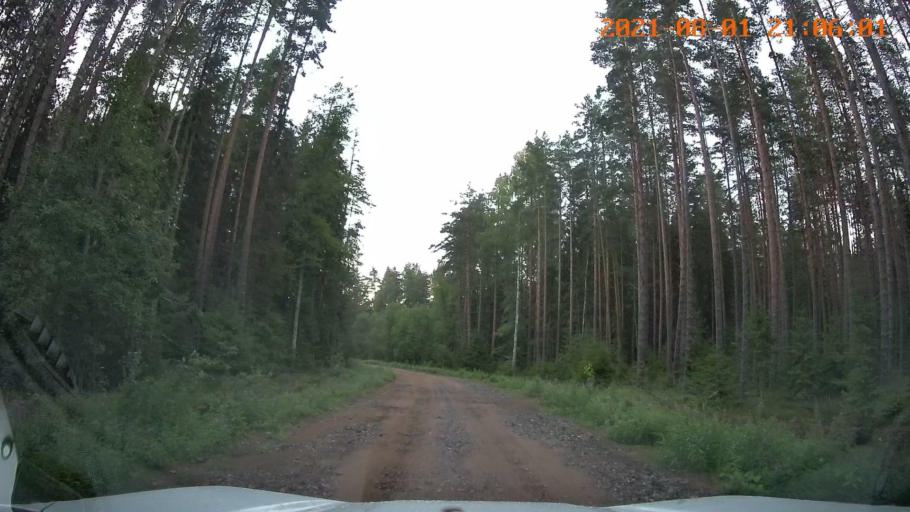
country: RU
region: Leningrad
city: Syas'stroy
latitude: 60.4999
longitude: 32.6506
